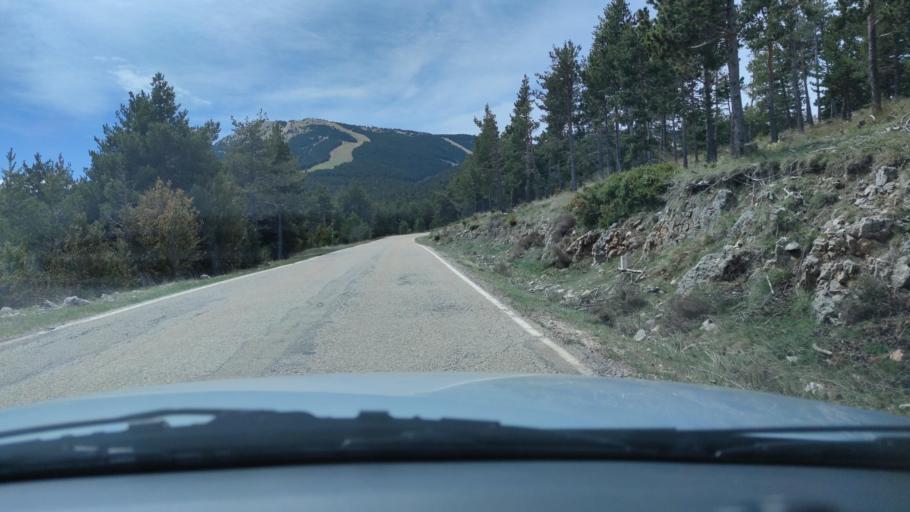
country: ES
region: Catalonia
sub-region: Provincia de Lleida
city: Gosol
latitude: 42.1833
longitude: 1.5589
